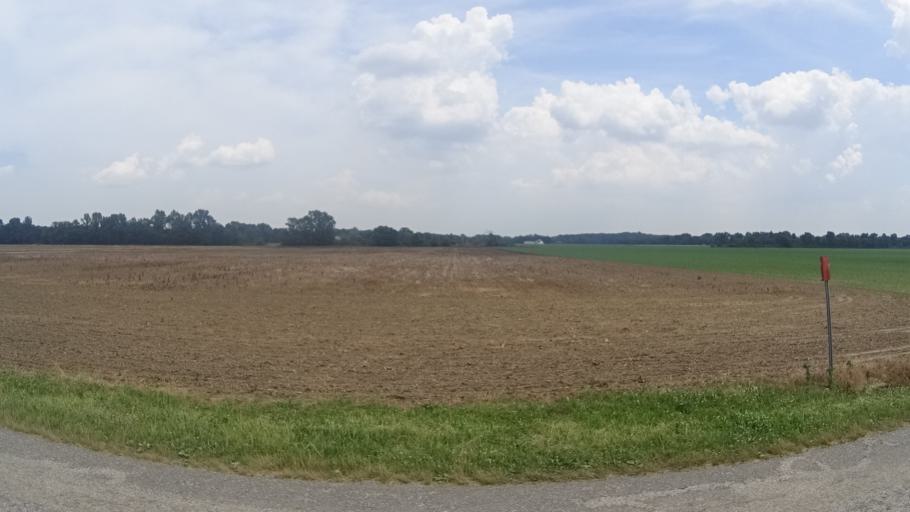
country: US
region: Ohio
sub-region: Huron County
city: Monroeville
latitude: 41.2973
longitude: -82.6719
